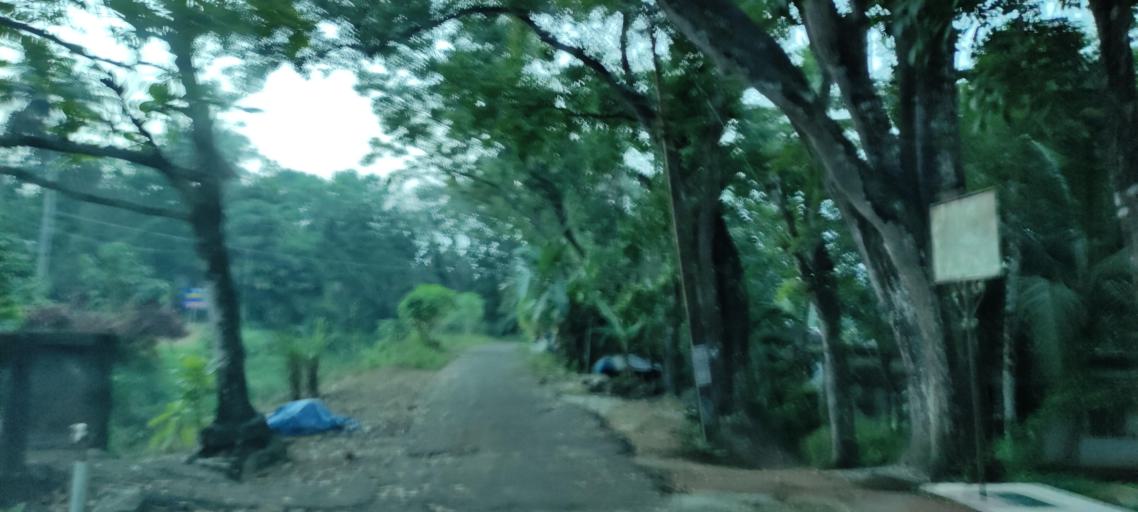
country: IN
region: Kerala
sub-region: Pattanamtitta
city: Adur
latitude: 9.1605
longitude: 76.7512
